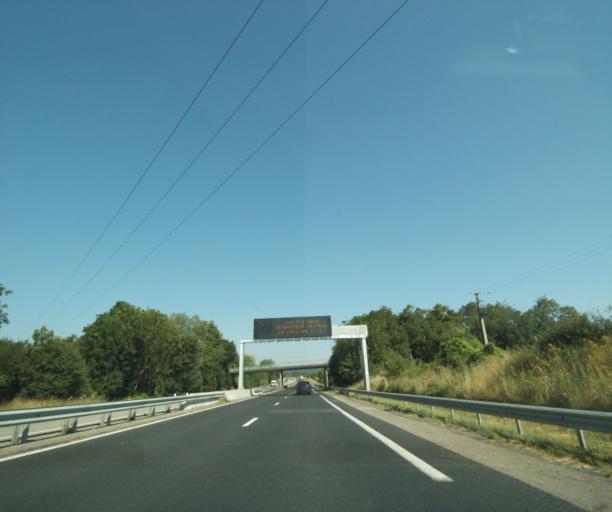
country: FR
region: Lorraine
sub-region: Departement de Meurthe-et-Moselle
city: Domgermain
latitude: 48.6621
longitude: 5.8328
